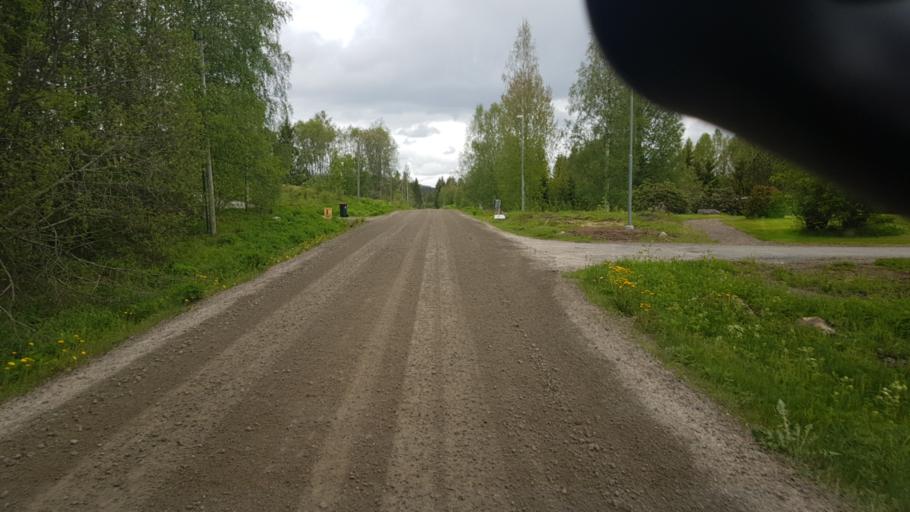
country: SE
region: Vaermland
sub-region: Arvika Kommun
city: Arvika
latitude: 59.7888
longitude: 12.7596
